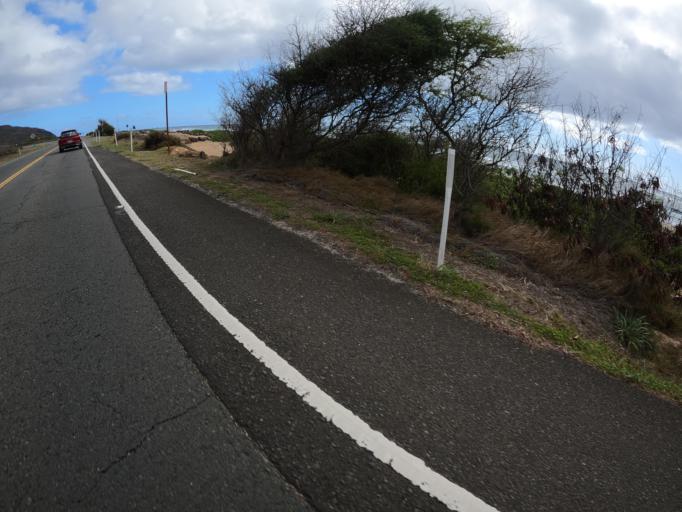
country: US
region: Hawaii
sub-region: Honolulu County
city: Waimanalo Beach
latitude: 21.2913
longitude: -157.6638
